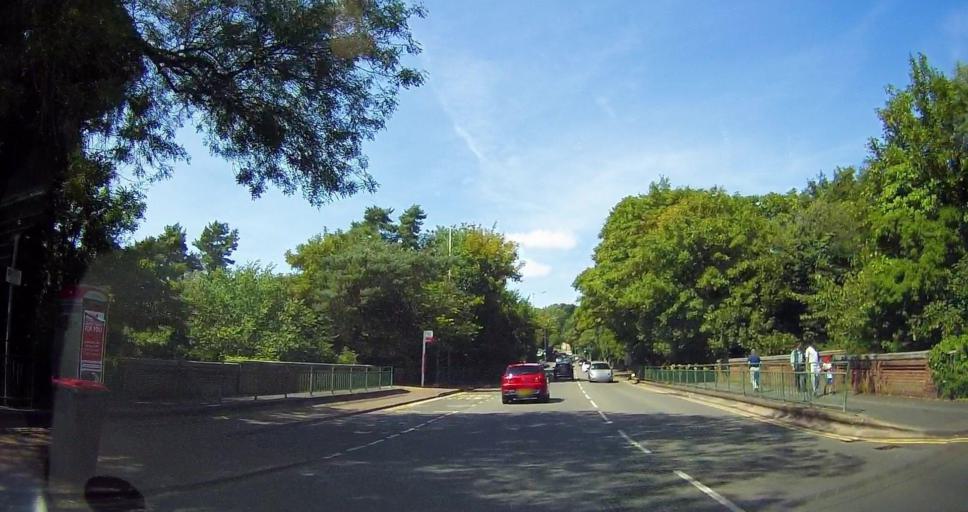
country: GB
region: England
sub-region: Wolverhampton
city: Wolverhampton
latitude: 52.5968
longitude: -2.1595
